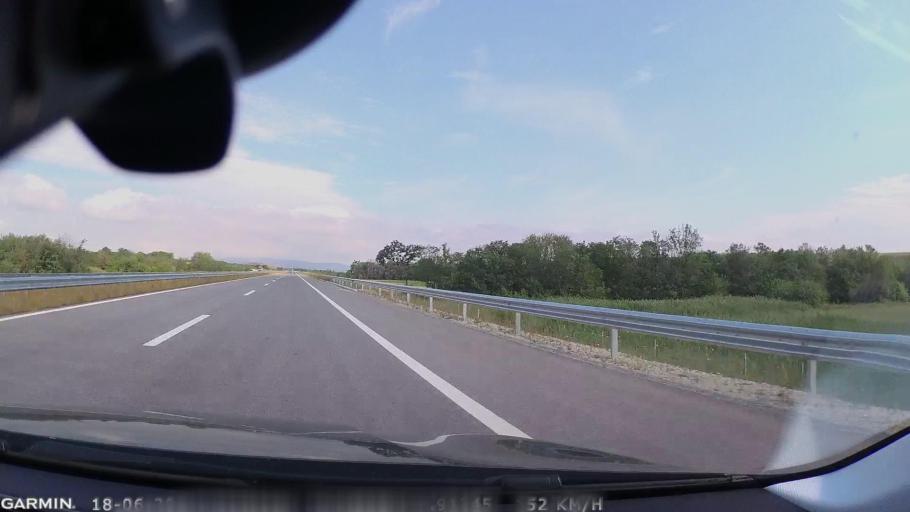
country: MK
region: Sveti Nikole
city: Gorobinci
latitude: 41.9030
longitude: 21.9122
